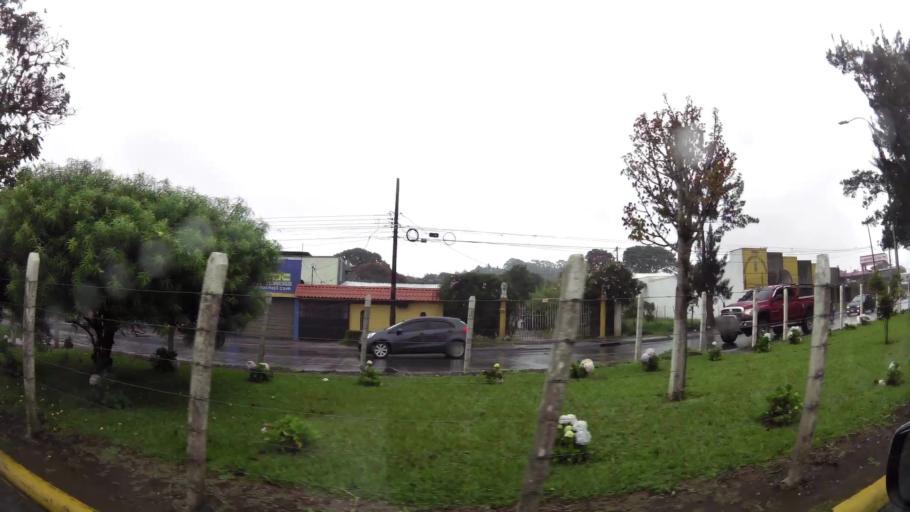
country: CR
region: Cartago
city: Cartago
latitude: 9.8666
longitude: -83.9335
